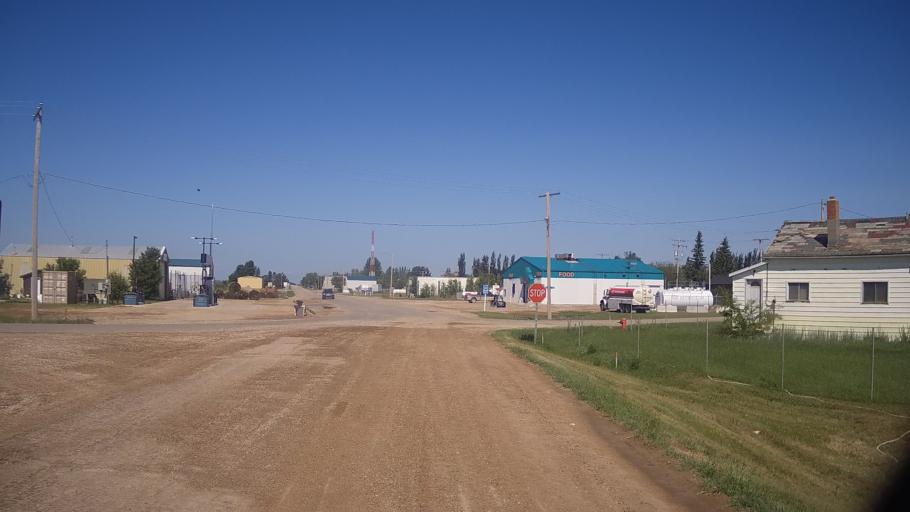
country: CA
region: Saskatchewan
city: Watrous
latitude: 51.8911
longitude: -106.0509
